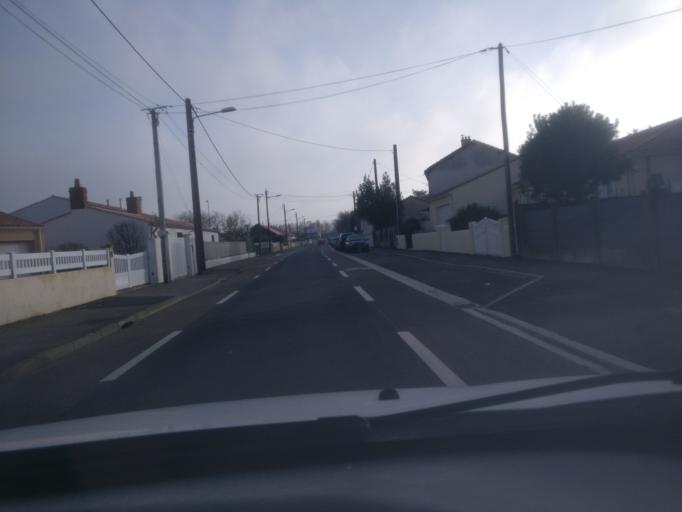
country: FR
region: Pays de la Loire
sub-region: Departement de la Loire-Atlantique
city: Saint-Sebastien-sur-Loire
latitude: 47.1965
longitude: -1.4912
